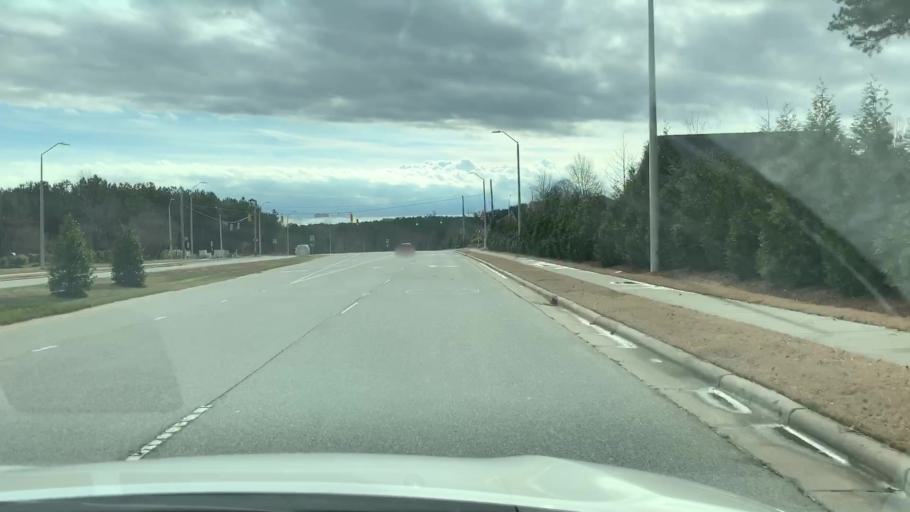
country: US
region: North Carolina
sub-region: Wake County
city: Green Level
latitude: 35.8199
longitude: -78.9026
